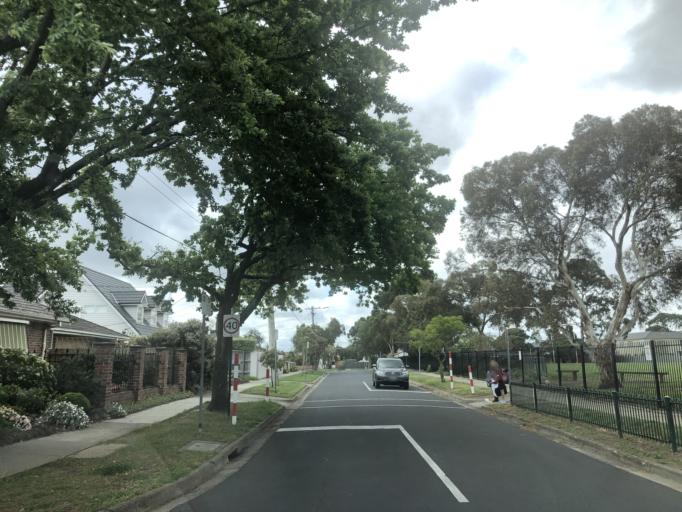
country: AU
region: Victoria
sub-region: Monash
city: Ashwood
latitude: -37.8814
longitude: 145.1222
